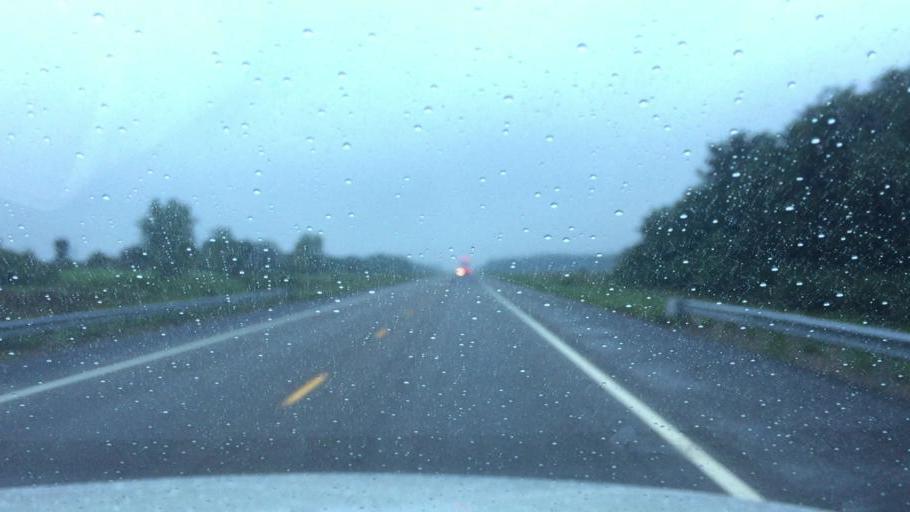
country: US
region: Kansas
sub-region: Montgomery County
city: Cherryvale
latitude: 37.4266
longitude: -95.4922
